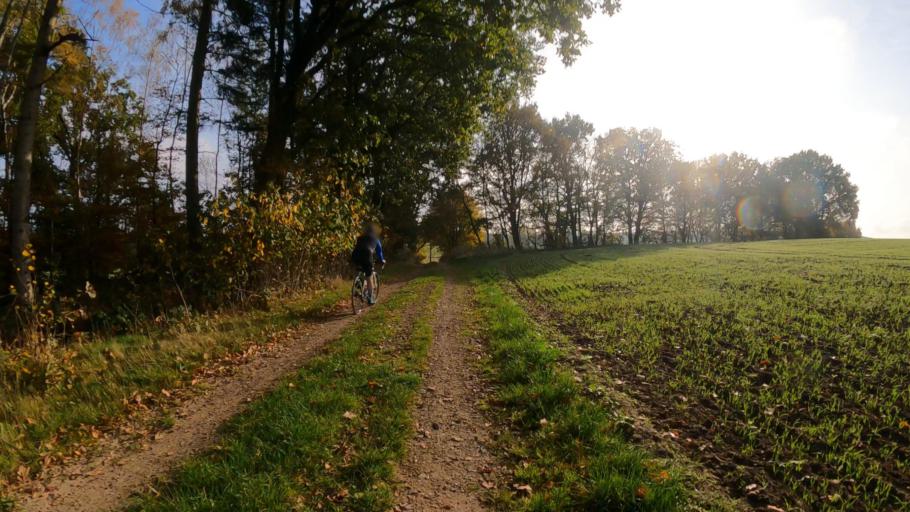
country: DE
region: Lower Saxony
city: Buchholz in der Nordheide
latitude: 53.3386
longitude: 9.8275
